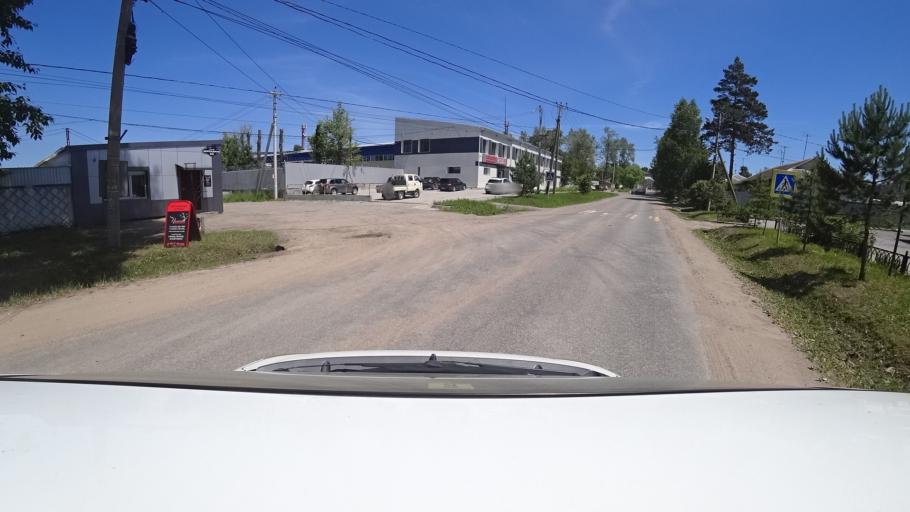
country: RU
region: Khabarovsk Krai
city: Topolevo
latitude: 48.5069
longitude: 135.1681
